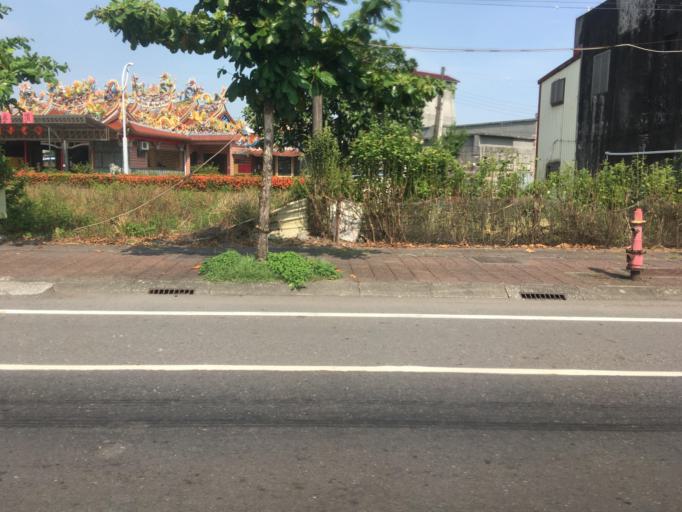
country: TW
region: Taiwan
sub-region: Yilan
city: Yilan
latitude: 24.6417
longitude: 121.8346
